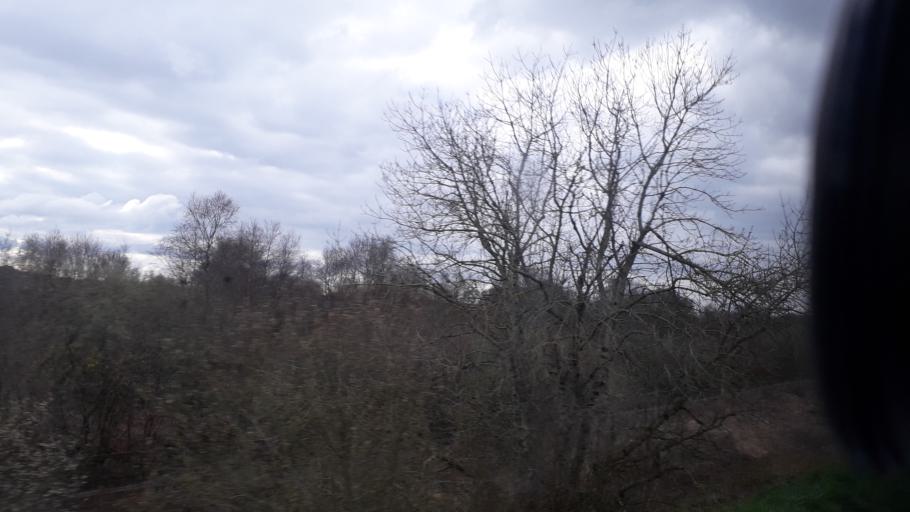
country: IE
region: Leinster
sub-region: An Longfort
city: Granard
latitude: 53.6542
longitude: -7.4370
